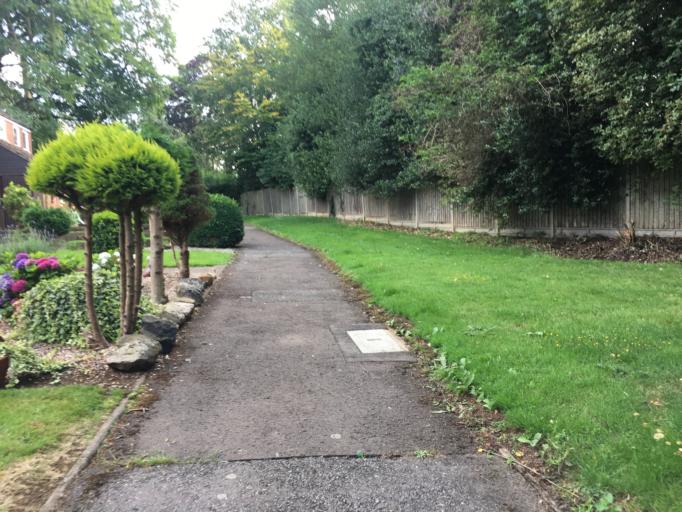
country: GB
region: England
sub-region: Warwickshire
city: Rugby
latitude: 52.3836
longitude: -1.2198
